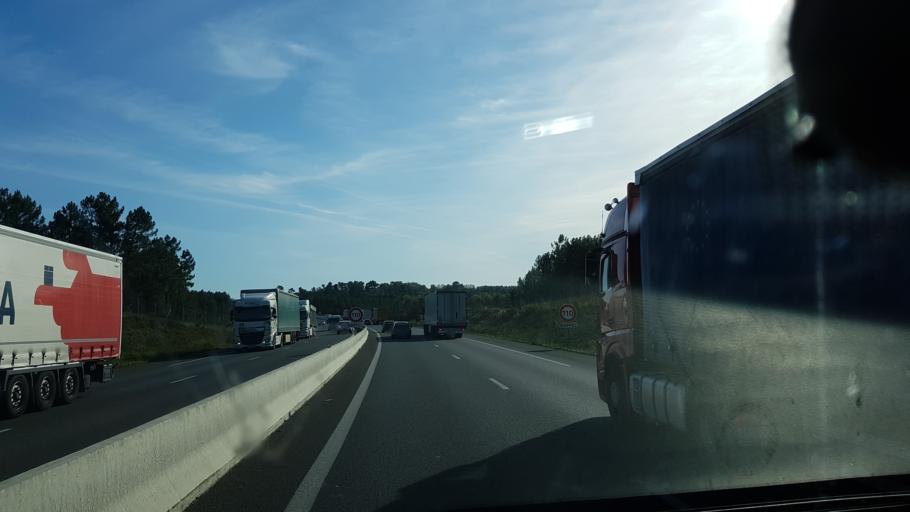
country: FR
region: Poitou-Charentes
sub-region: Departement de la Charente
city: Baignes-Sainte-Radegonde
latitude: 45.3816
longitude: -0.1816
